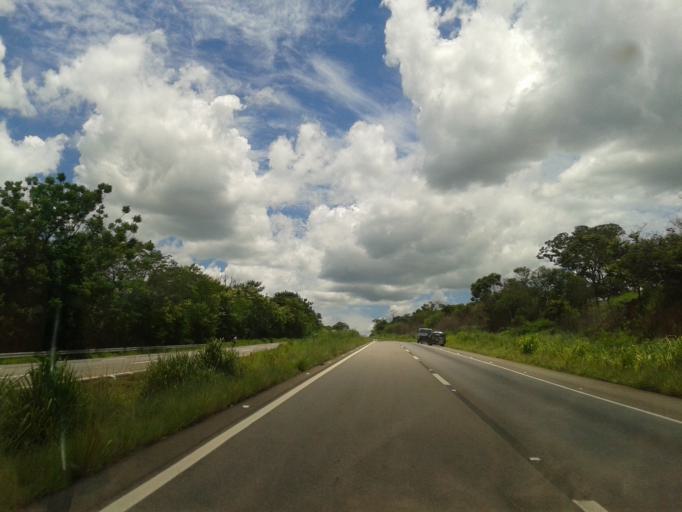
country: BR
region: Goias
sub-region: Neropolis
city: Neropolis
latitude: -16.3540
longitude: -49.2477
